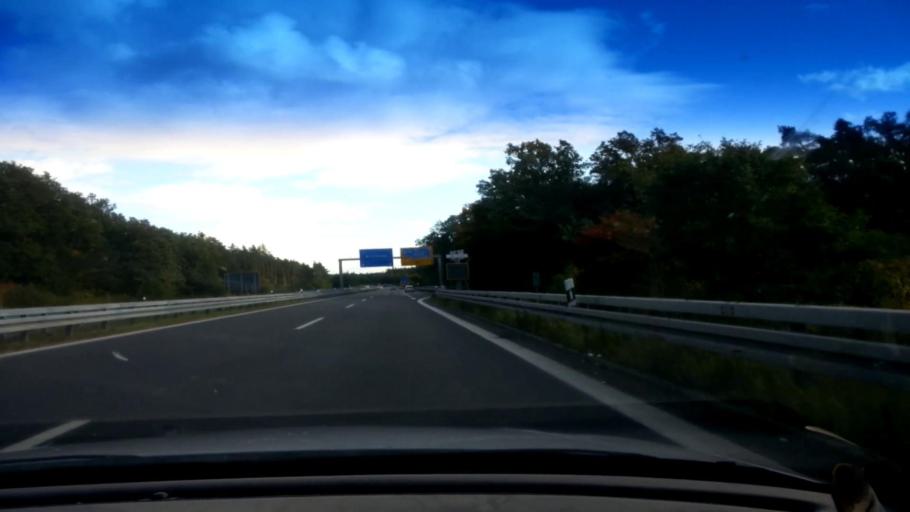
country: DE
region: Bavaria
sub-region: Upper Franconia
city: Bamberg
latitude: 49.8764
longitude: 10.9317
